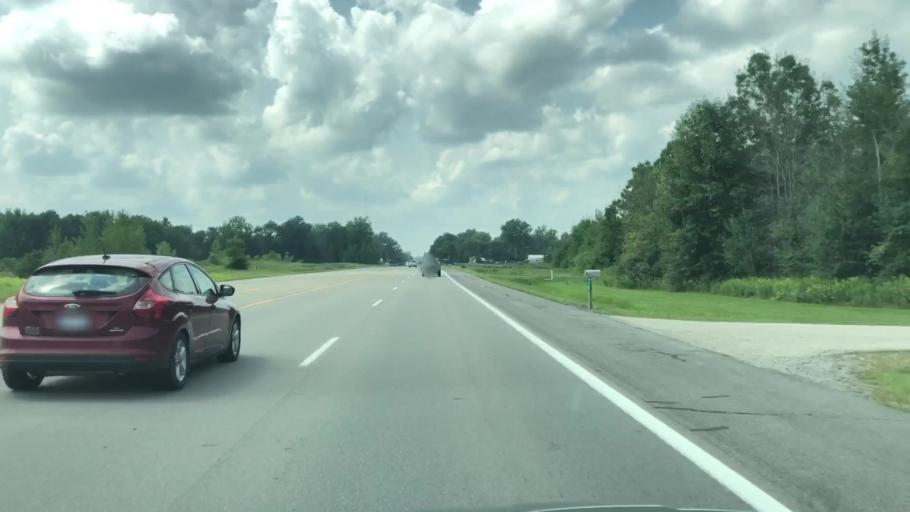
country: US
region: Michigan
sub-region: Midland County
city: Coleman
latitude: 43.6116
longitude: -84.5211
